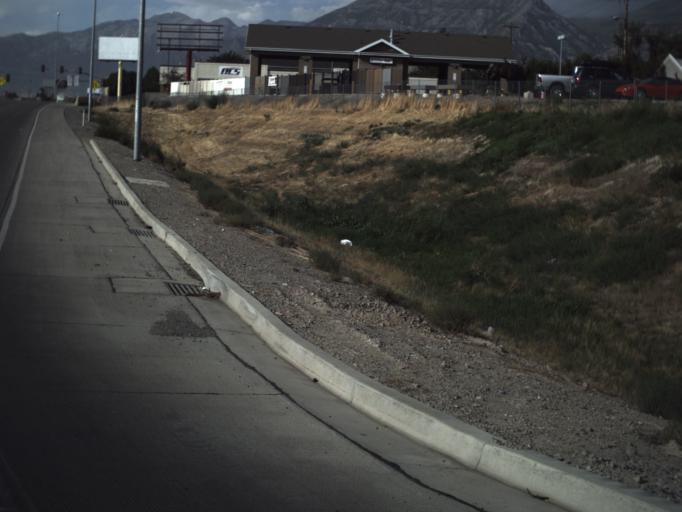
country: US
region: Utah
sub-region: Utah County
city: Orem
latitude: 40.2975
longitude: -111.7247
